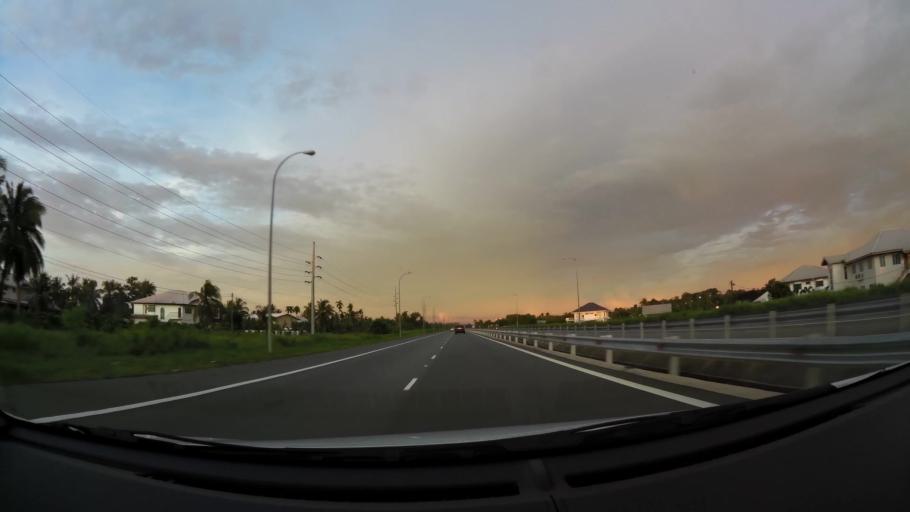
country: BN
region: Belait
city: Kuala Belait
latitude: 4.5806
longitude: 114.2444
